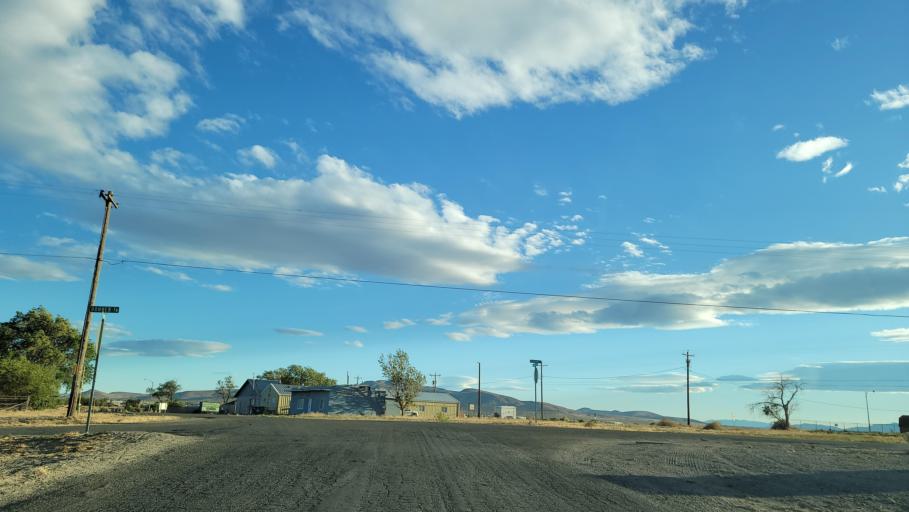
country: US
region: Nevada
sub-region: Lyon County
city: Silver Springs
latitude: 39.4145
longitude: -119.2234
